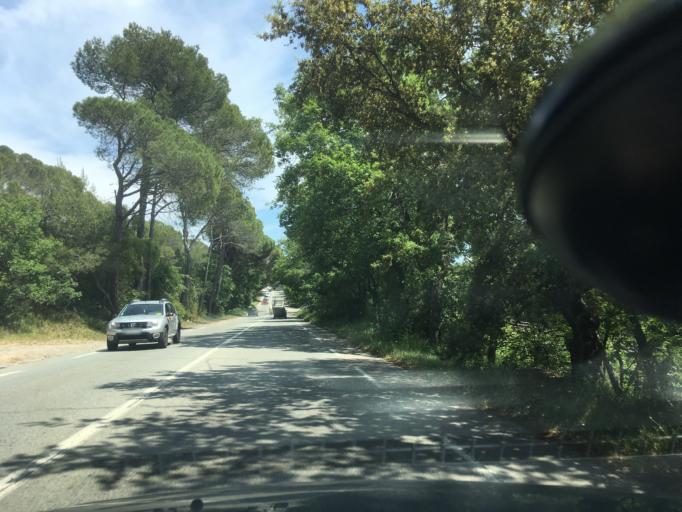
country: FR
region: Provence-Alpes-Cote d'Azur
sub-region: Departement du Var
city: Puget-sur-Argens
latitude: 43.4605
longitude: 6.6623
